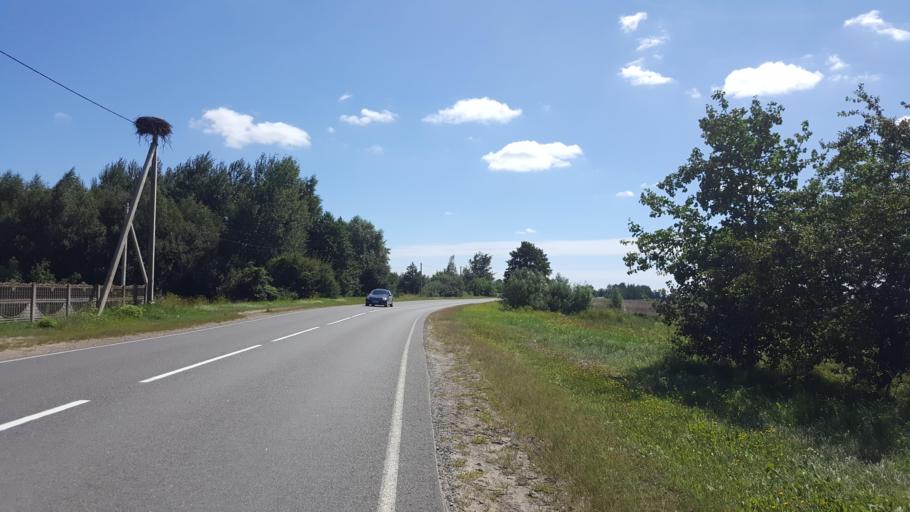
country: BY
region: Brest
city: Kobryn
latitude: 52.3523
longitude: 24.1895
